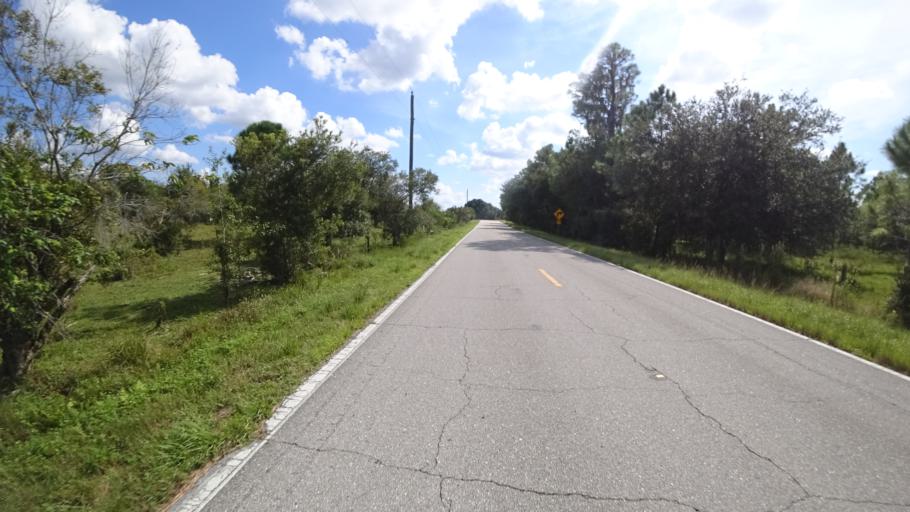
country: US
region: Florida
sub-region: Hardee County
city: Wauchula
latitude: 27.4963
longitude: -82.0707
